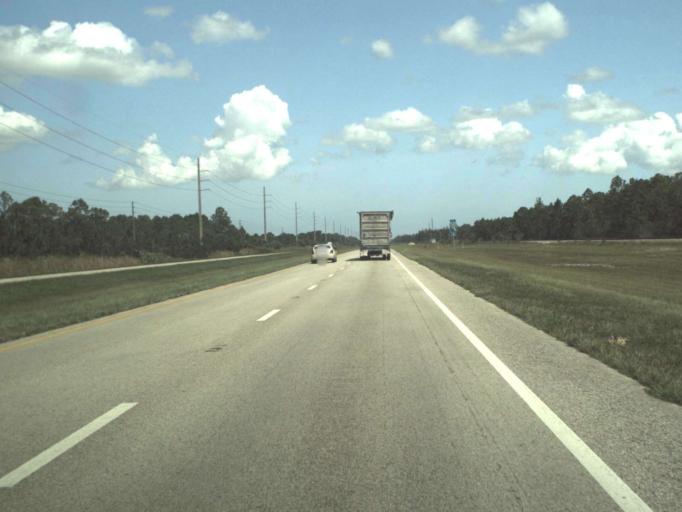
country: US
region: Florida
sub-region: Palm Beach County
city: Palm Beach Gardens
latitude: 26.8622
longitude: -80.2308
